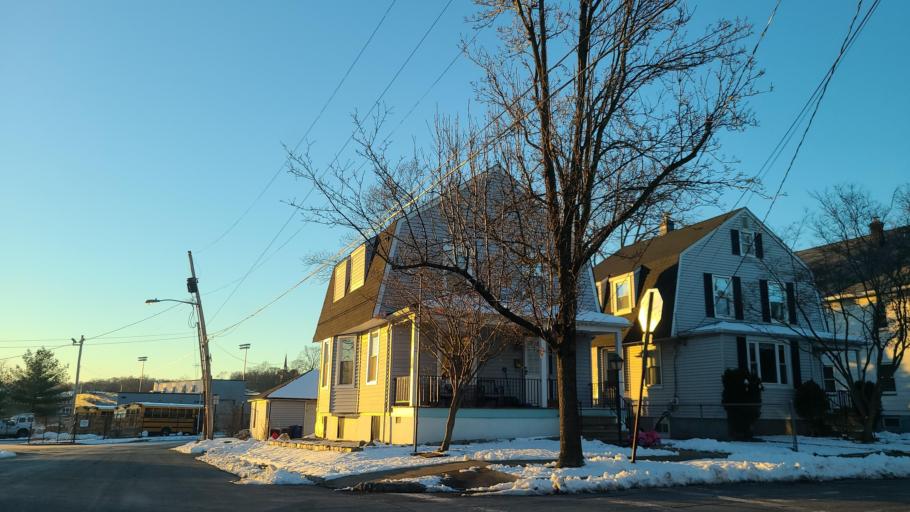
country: US
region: New Jersey
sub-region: Union County
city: Springfield
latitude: 40.7207
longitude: -74.3117
